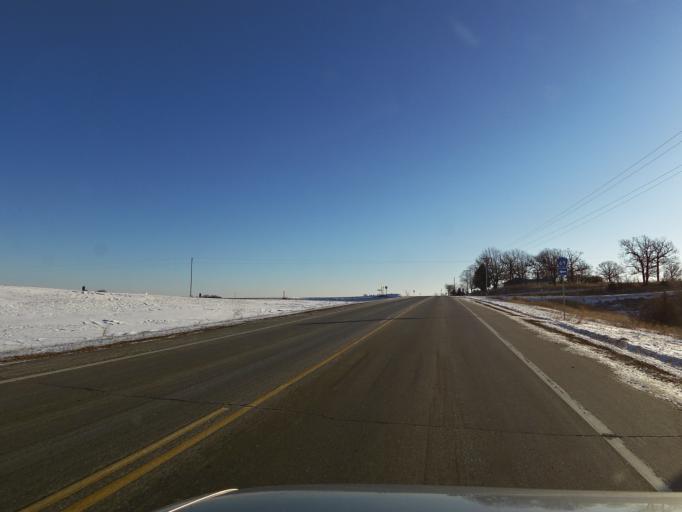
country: US
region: Minnesota
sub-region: Carver County
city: Chaska
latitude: 44.7326
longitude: -93.5639
